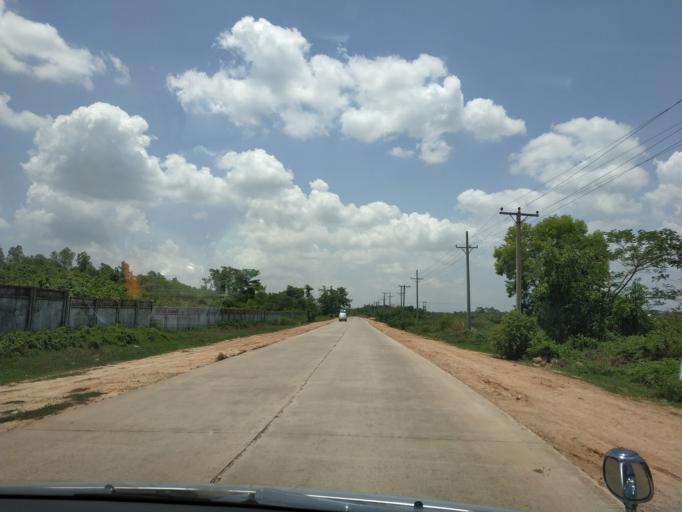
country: MM
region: Bago
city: Bago
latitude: 17.4685
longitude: 96.4584
